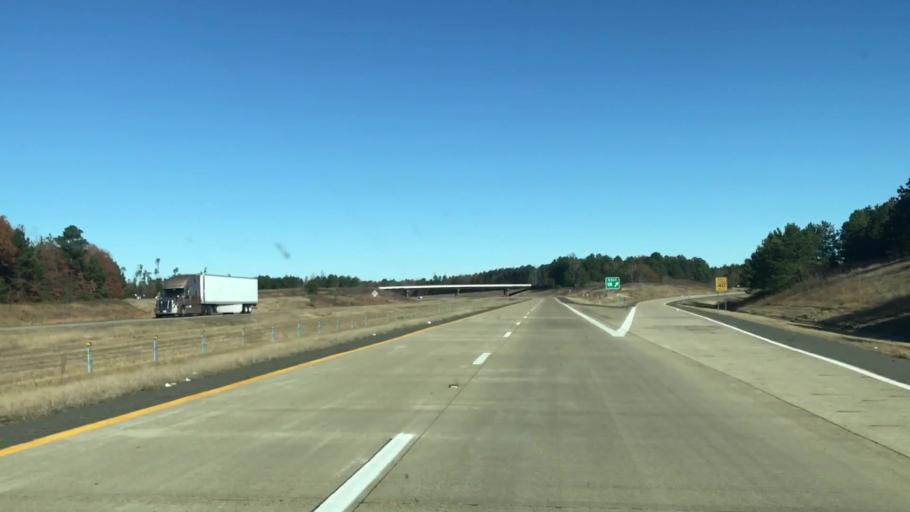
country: US
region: Texas
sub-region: Bowie County
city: Texarkana
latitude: 33.2645
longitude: -93.8974
